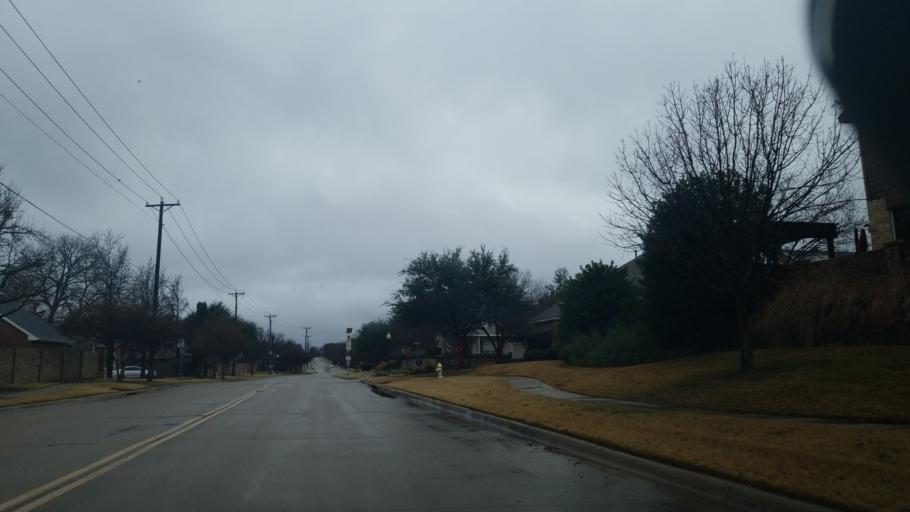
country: US
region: Texas
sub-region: Denton County
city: Corinth
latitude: 33.1507
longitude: -97.0852
